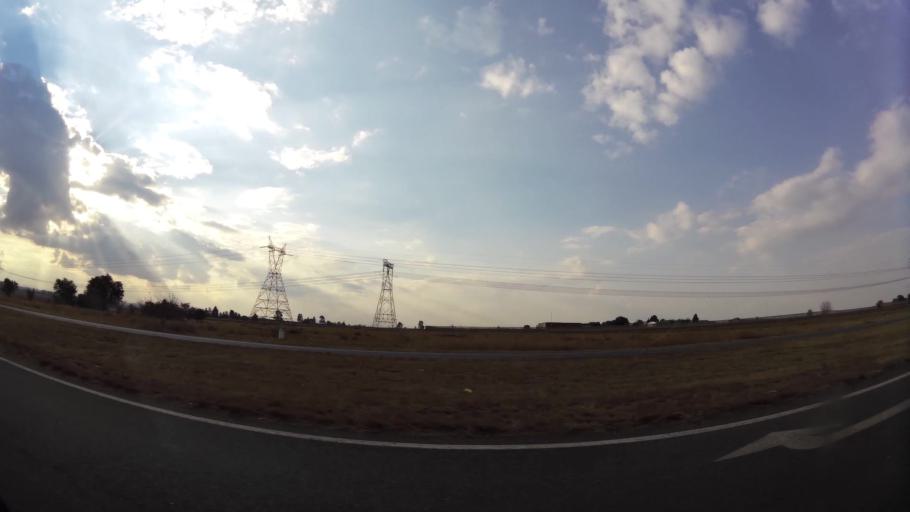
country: ZA
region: Gauteng
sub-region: Sedibeng District Municipality
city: Vanderbijlpark
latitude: -26.6187
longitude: 27.8335
